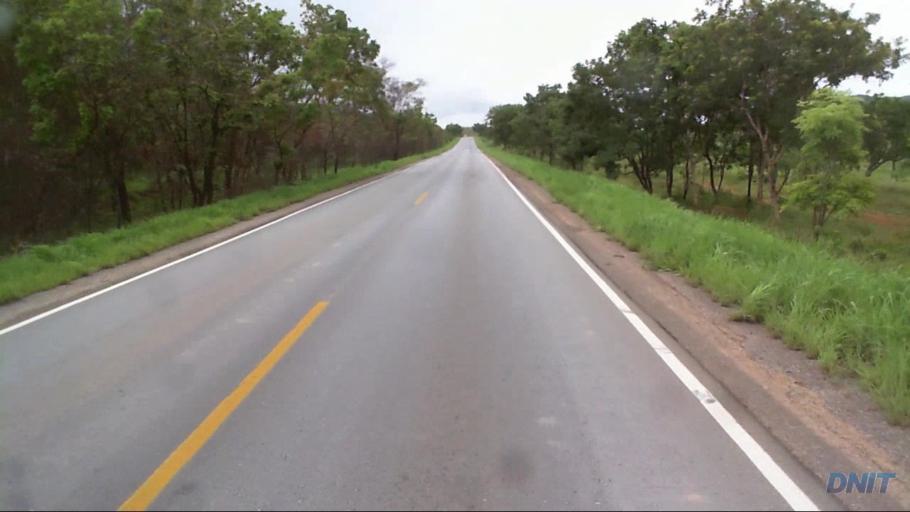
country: BR
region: Goias
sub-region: Padre Bernardo
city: Padre Bernardo
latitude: -15.4521
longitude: -48.2099
